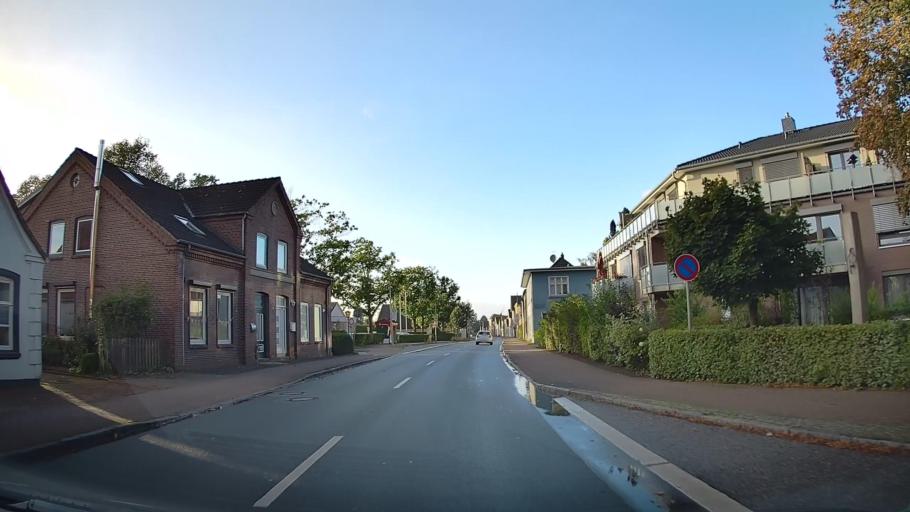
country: DE
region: Schleswig-Holstein
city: Horst
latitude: 53.8116
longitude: 9.6173
